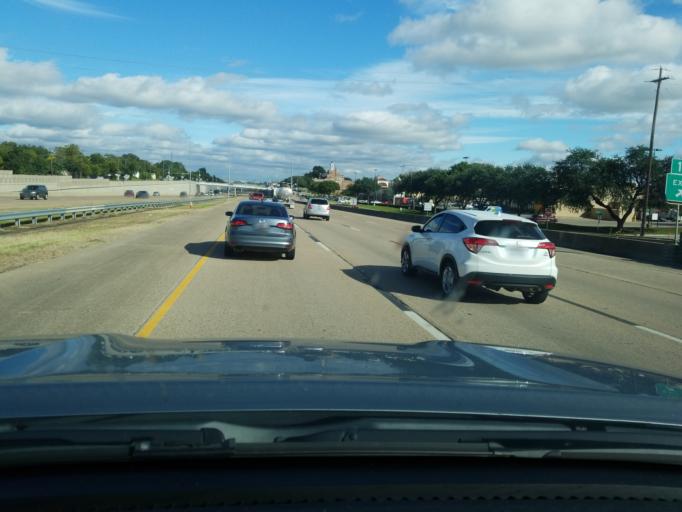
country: US
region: Texas
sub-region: Tarrant County
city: Westworth
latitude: 32.7330
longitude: -97.3923
